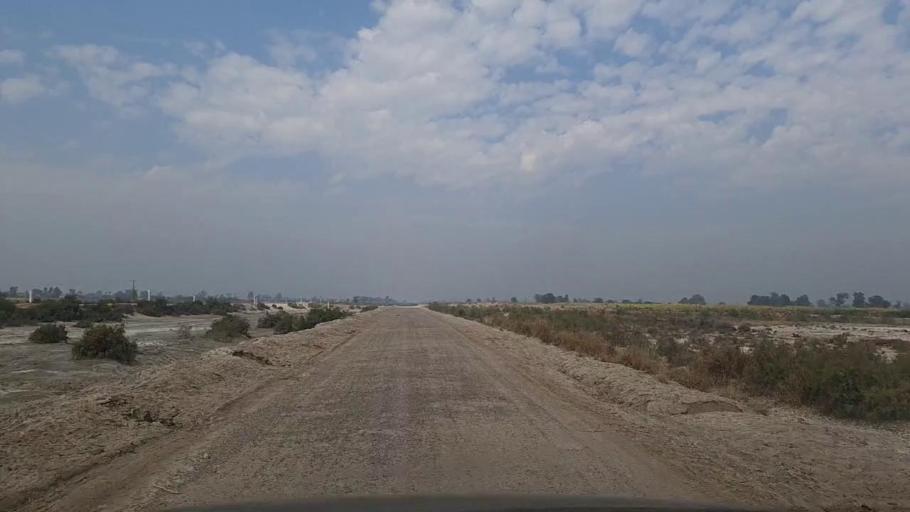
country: PK
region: Sindh
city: Daur
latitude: 26.3674
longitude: 68.3602
